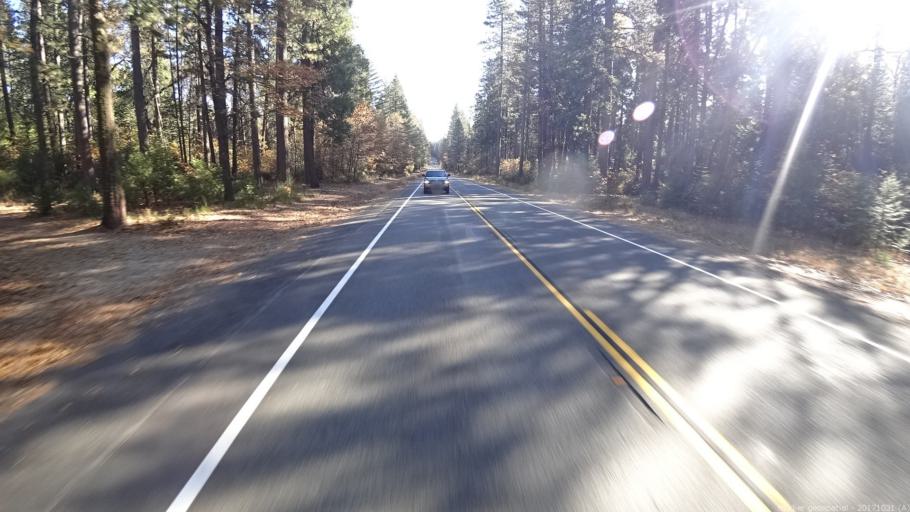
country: US
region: California
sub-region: Shasta County
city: Shingletown
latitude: 40.4946
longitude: -121.8712
